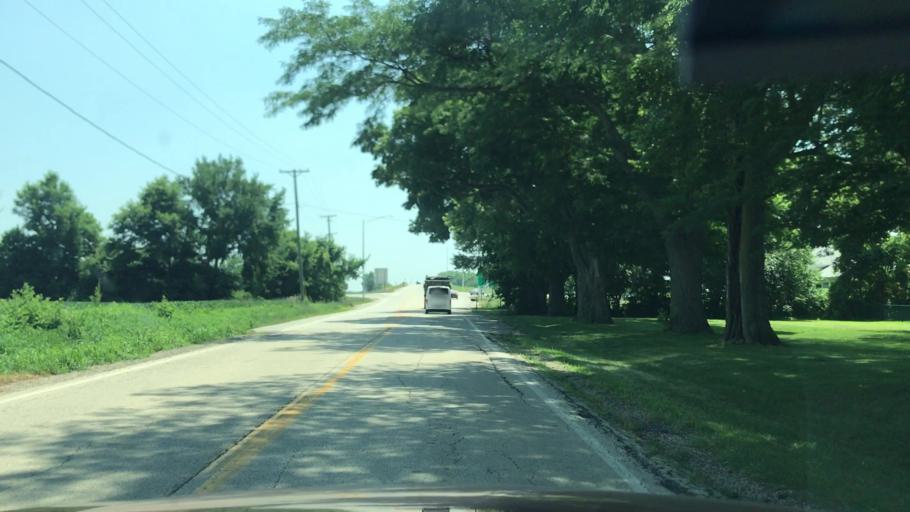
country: US
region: Illinois
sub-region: Winnebago County
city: Cherry Valley
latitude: 42.2371
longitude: -88.9007
